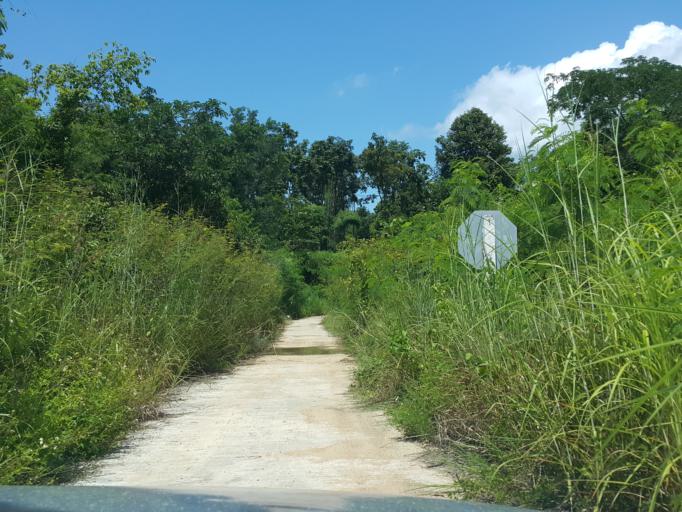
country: TH
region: Chiang Mai
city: San Kamphaeng
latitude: 18.7018
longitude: 99.1783
